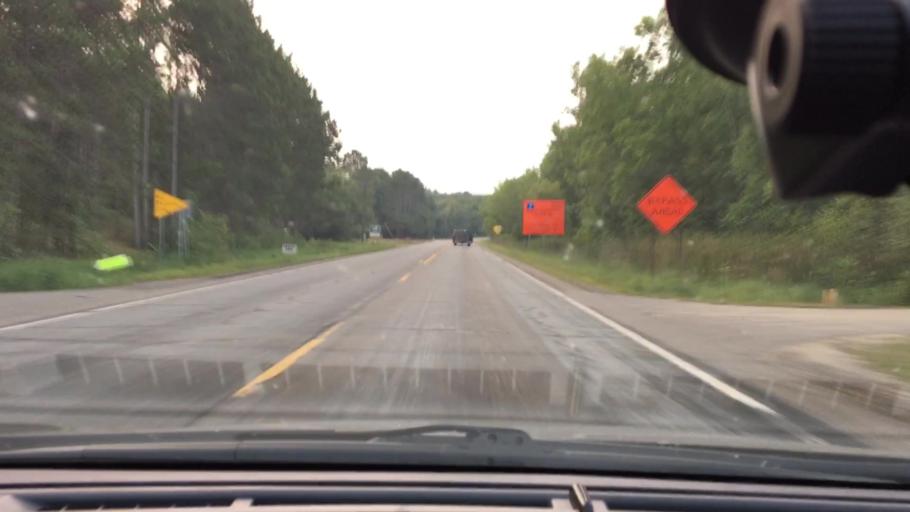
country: US
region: Minnesota
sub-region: Crow Wing County
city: Cross Lake
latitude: 46.7212
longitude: -93.9566
